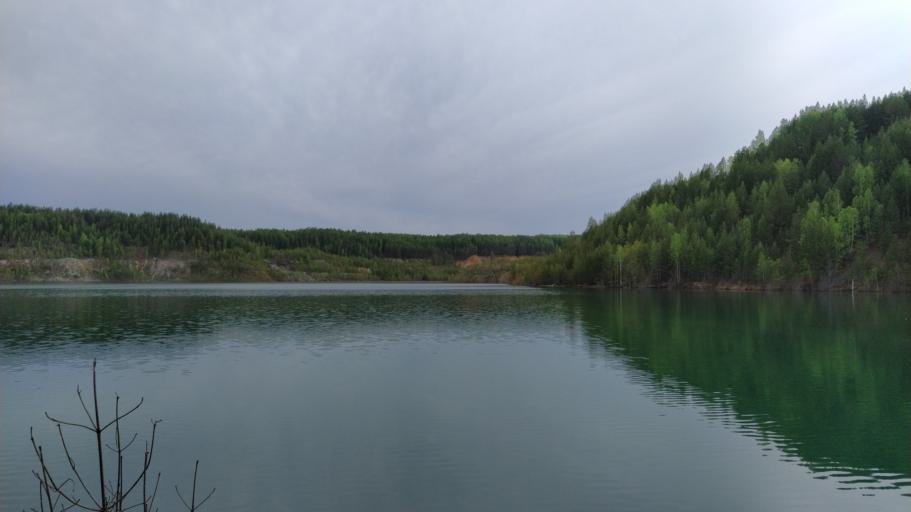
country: RU
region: Sverdlovsk
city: Losinyy
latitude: 57.4331
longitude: 61.1085
